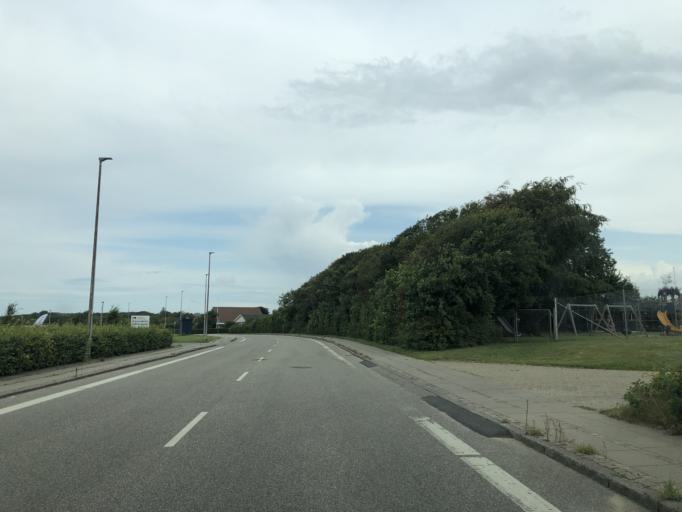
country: DK
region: Central Jutland
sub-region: Ringkobing-Skjern Kommune
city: Ringkobing
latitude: 56.0942
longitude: 8.2617
